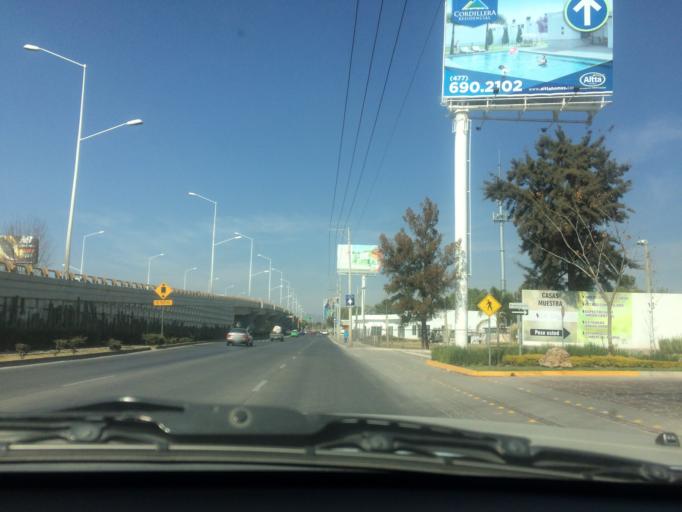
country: MX
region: Guanajuato
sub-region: Leon
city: Medina
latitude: 21.1699
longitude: -101.6557
